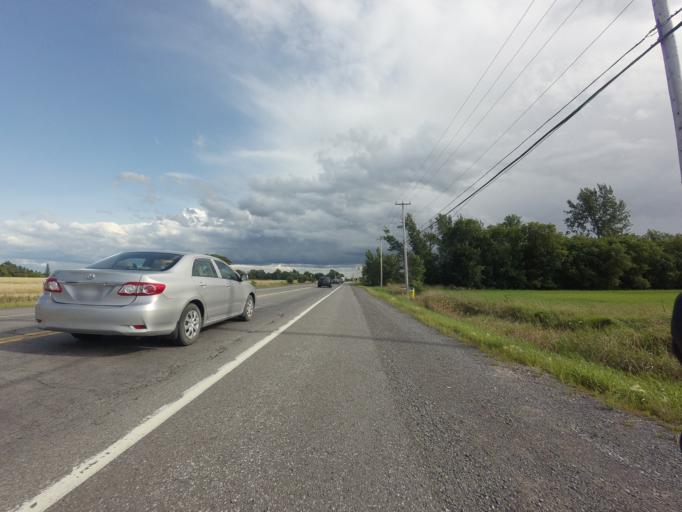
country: CA
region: Ontario
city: Ottawa
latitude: 45.3042
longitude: -75.7068
